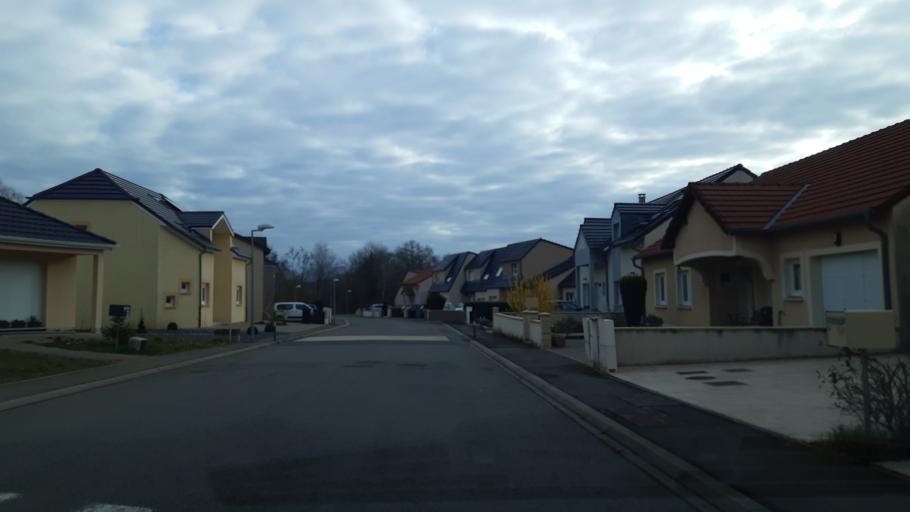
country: FR
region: Lorraine
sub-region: Departement de la Moselle
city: Russange
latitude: 49.4765
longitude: 5.9511
